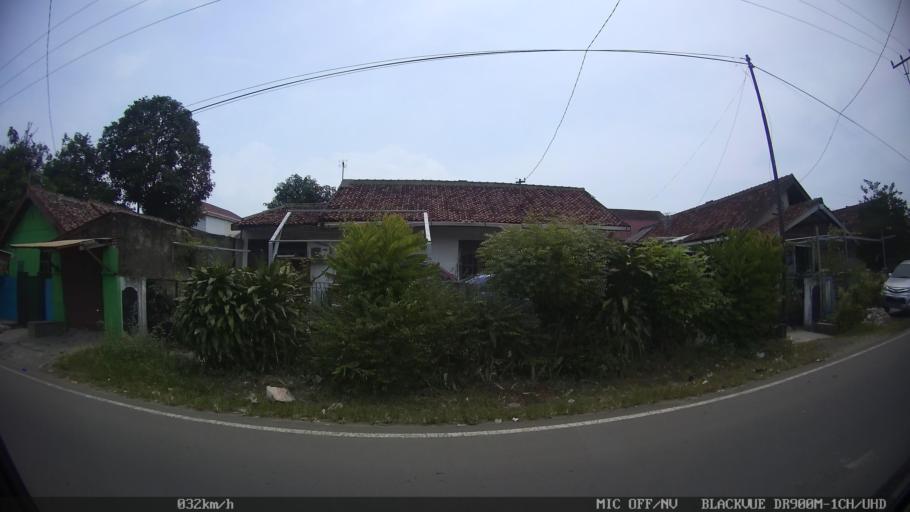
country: ID
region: Lampung
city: Bandarlampung
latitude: -5.4287
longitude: 105.2772
